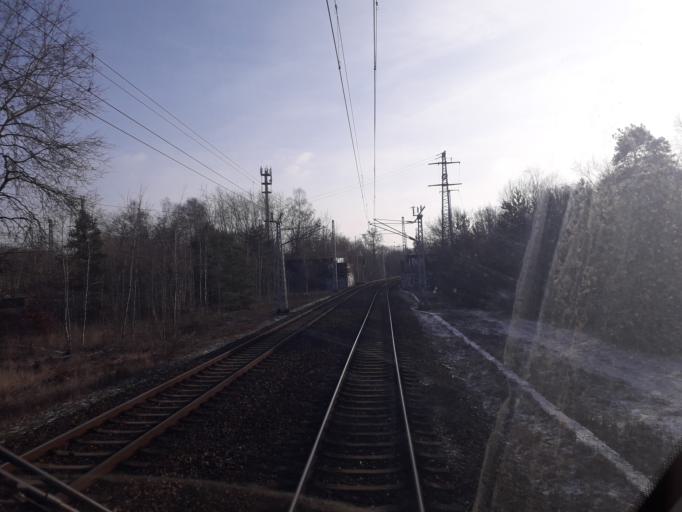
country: DE
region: Berlin
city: Karlshorst
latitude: 52.4709
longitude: 13.5480
